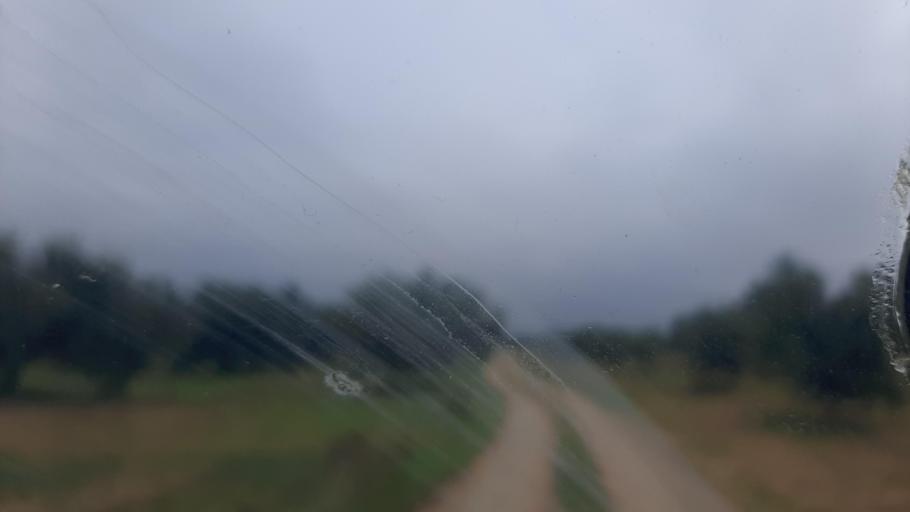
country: TN
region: Tunis
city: La Sebala du Mornag
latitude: 36.5793
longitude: 10.2900
